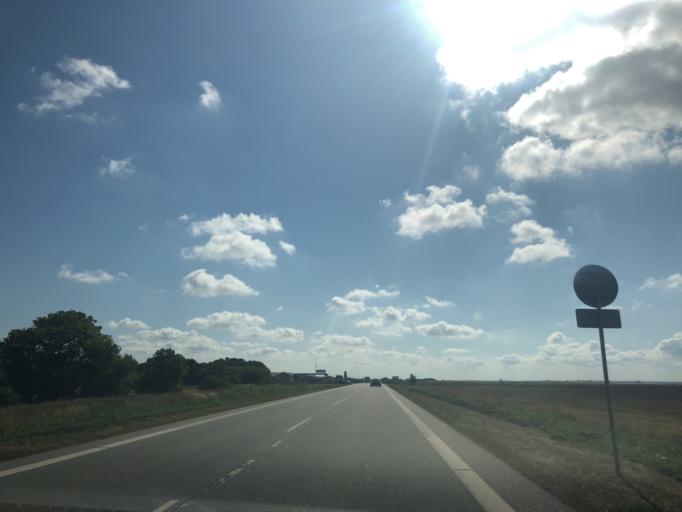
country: DK
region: North Denmark
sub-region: Vesthimmerland Kommune
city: Logstor
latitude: 57.0252
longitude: 9.0095
